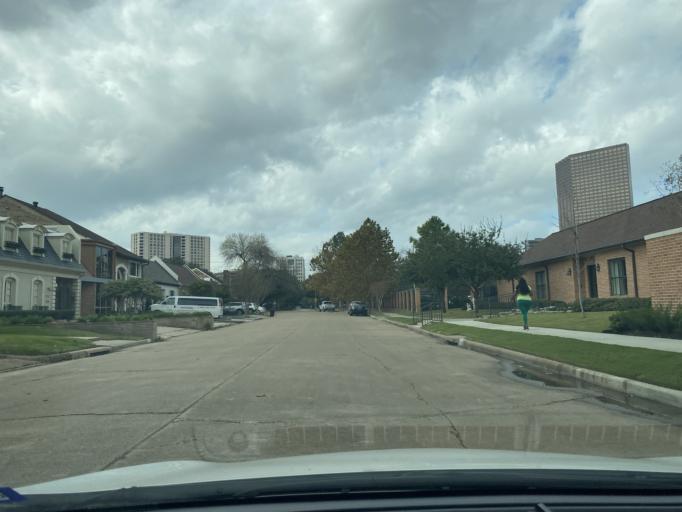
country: US
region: Texas
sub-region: Harris County
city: Hunters Creek Village
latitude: 29.7469
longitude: -95.4657
